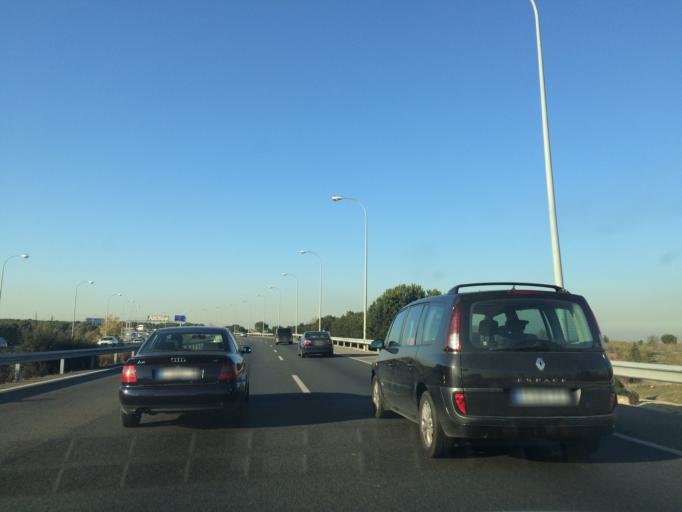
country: ES
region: Madrid
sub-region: Provincia de Madrid
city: Alcorcon
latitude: 40.3781
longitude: -3.8085
